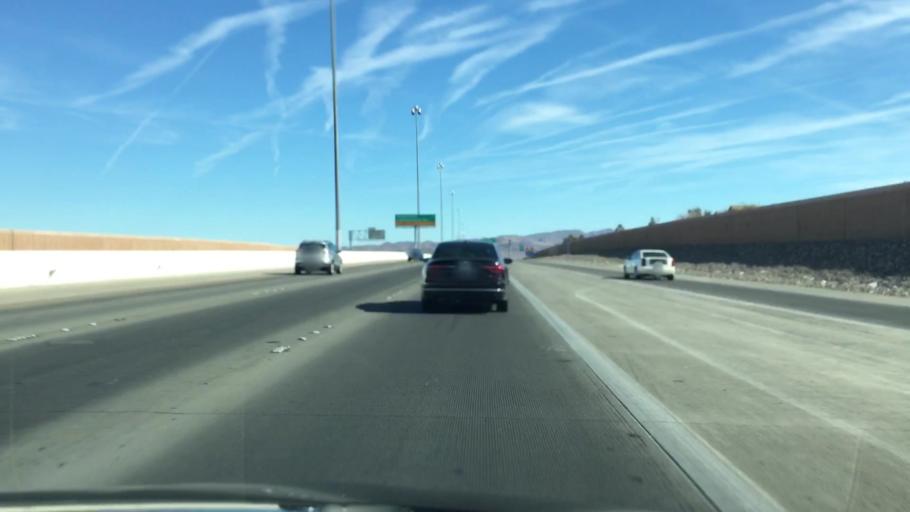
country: US
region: Nevada
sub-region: Clark County
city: Whitney
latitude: 36.0298
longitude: -115.0431
